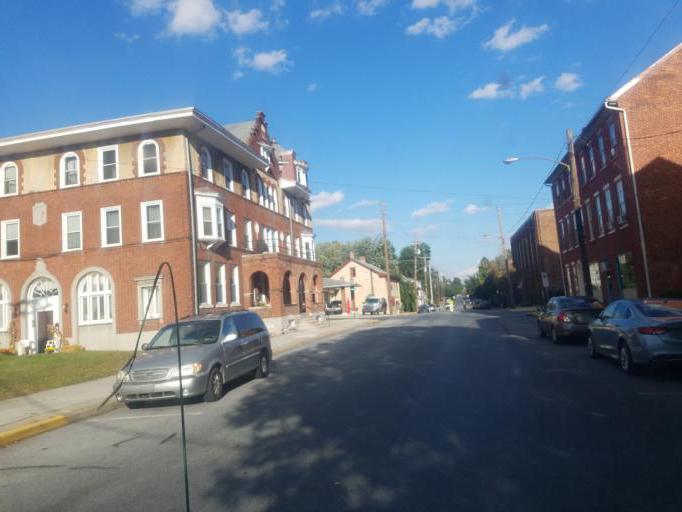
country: US
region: Pennsylvania
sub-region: Lancaster County
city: Marietta
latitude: 40.0571
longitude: -76.5529
